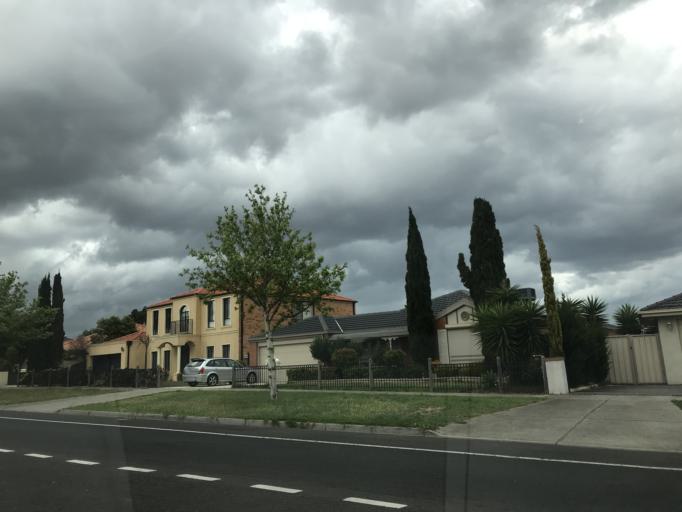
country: AU
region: Victoria
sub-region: Brimbank
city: Derrimut
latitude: -37.7924
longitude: 144.7686
